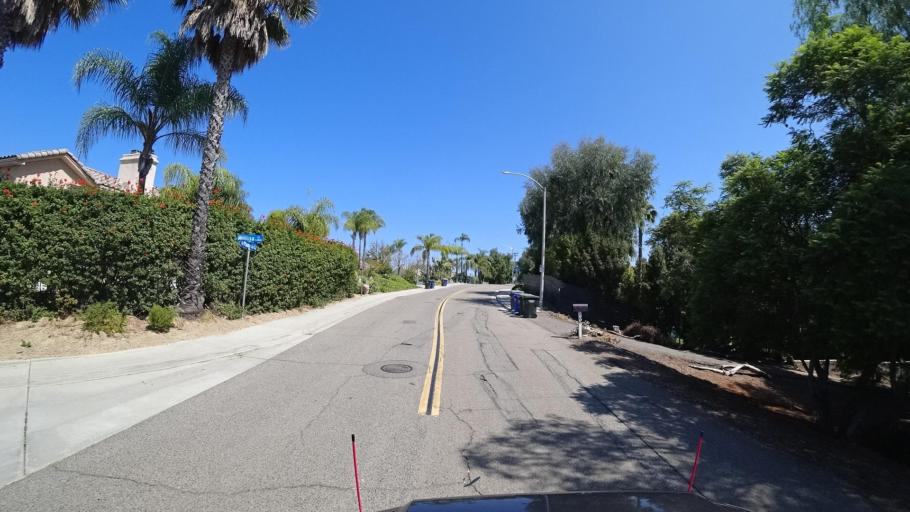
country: US
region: California
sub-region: San Diego County
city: Lake San Marcos
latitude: 33.1598
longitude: -117.2160
